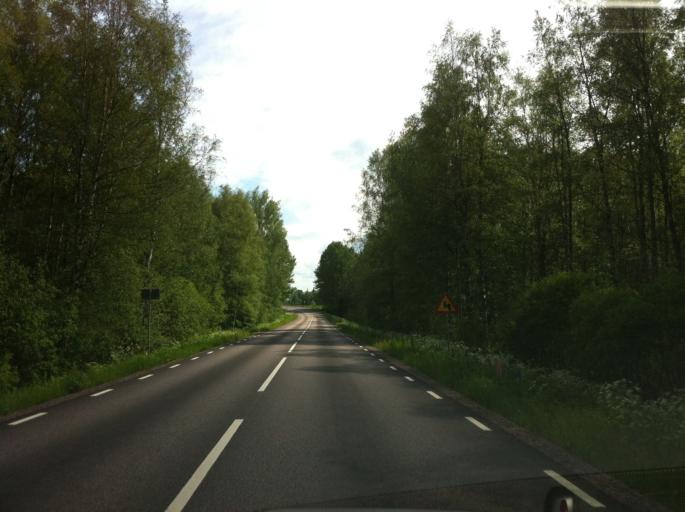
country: SE
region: Vaermland
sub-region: Sunne Kommun
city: Sunne
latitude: 59.8025
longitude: 13.0474
